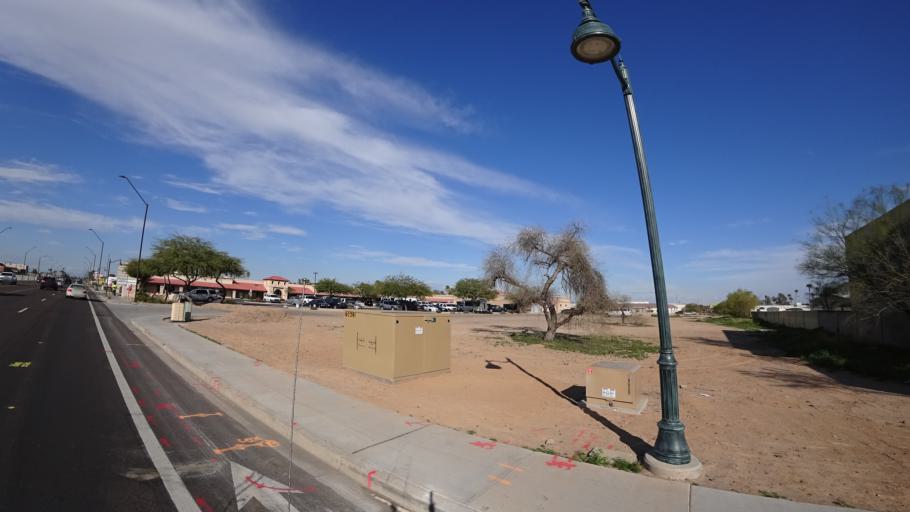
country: US
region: Arizona
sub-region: Maricopa County
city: Avondale
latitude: 33.4422
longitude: -112.3410
